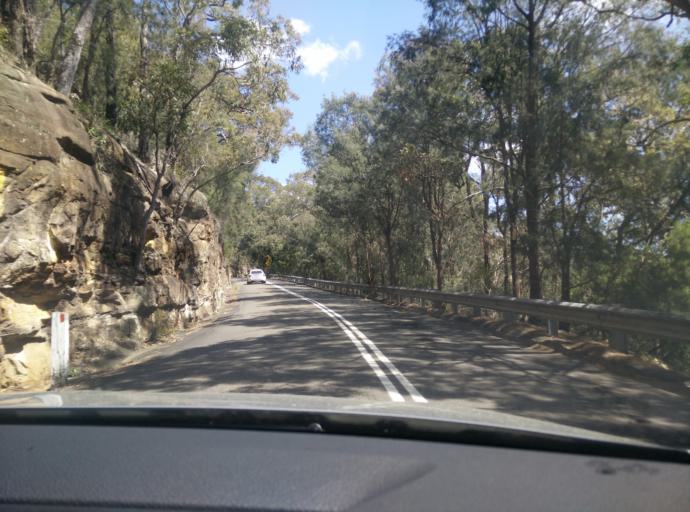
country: AU
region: New South Wales
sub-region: Gosford Shire
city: Umina
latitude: -33.5351
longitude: 151.3111
